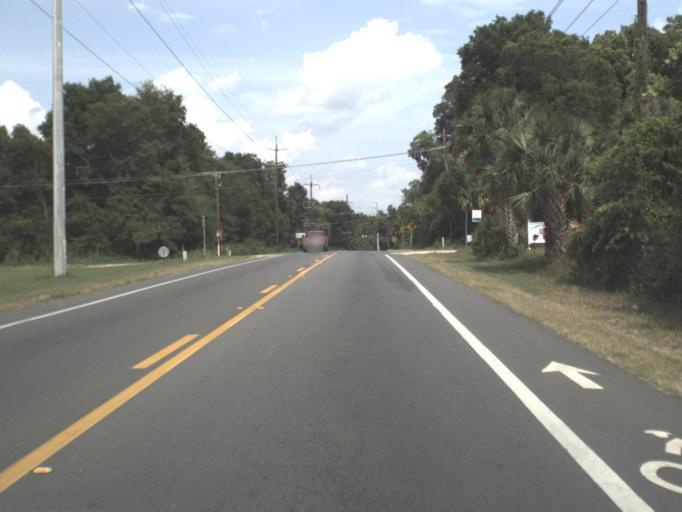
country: US
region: Florida
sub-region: Putnam County
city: Interlachen
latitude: 29.6260
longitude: -81.8960
